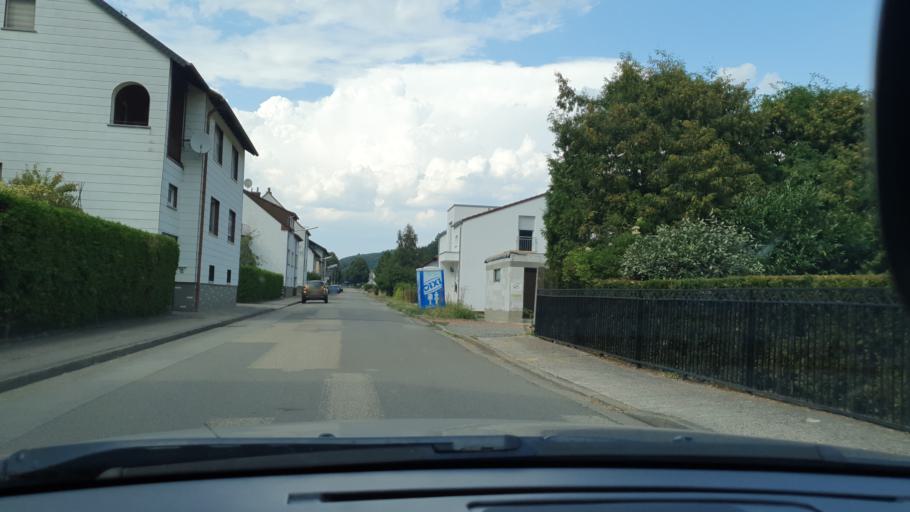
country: DE
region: Rheinland-Pfalz
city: Bechhofen
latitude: 49.3511
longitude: 7.4095
